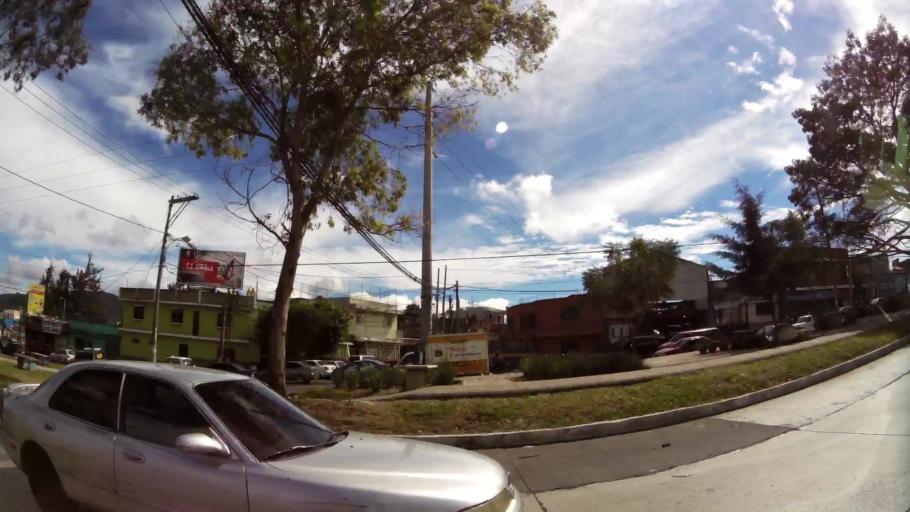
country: GT
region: Guatemala
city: Mixco
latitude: 14.6565
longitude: -90.5702
